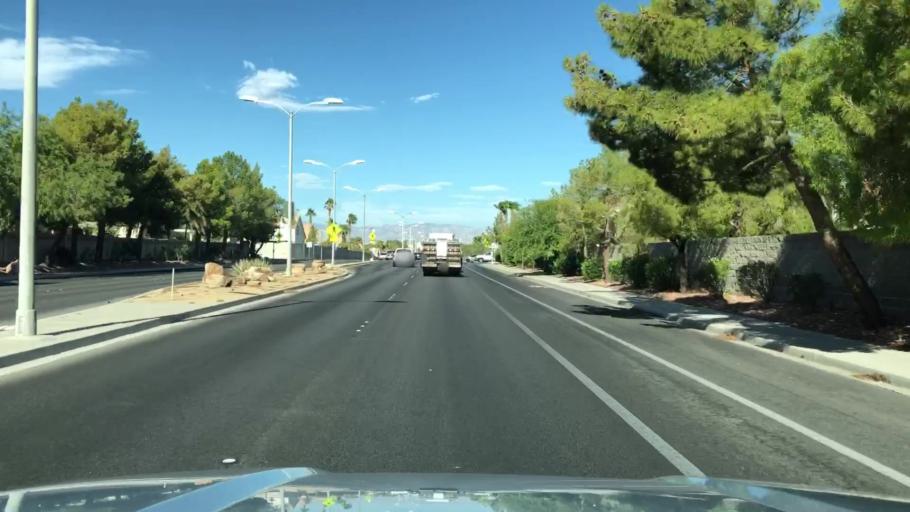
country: US
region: Nevada
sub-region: Clark County
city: Whitney
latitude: 36.0424
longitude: -115.1078
